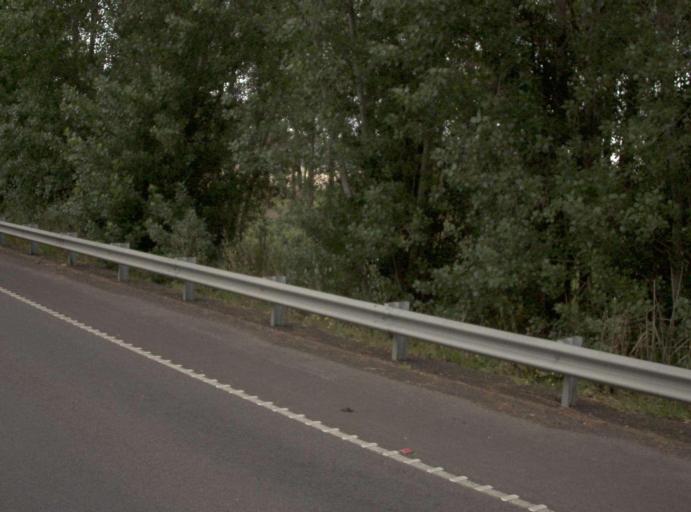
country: AU
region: Victoria
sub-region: Latrobe
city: Morwell
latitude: -38.2933
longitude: 146.4159
